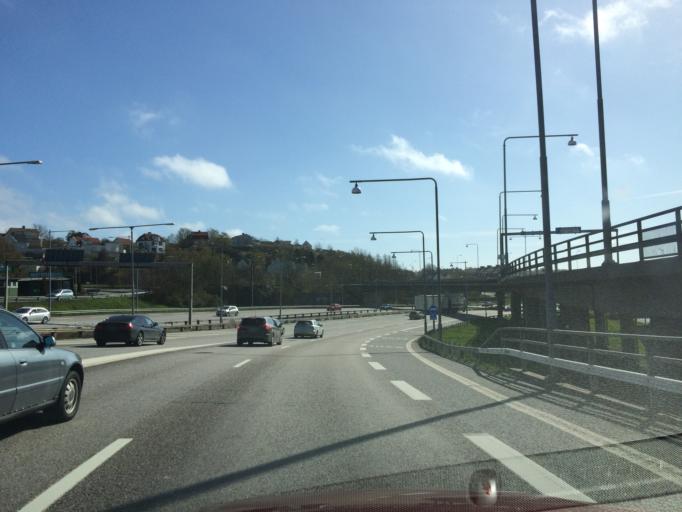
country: SE
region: Vaestra Goetaland
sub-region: Goteborg
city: Majorna
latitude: 57.6820
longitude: 11.9043
